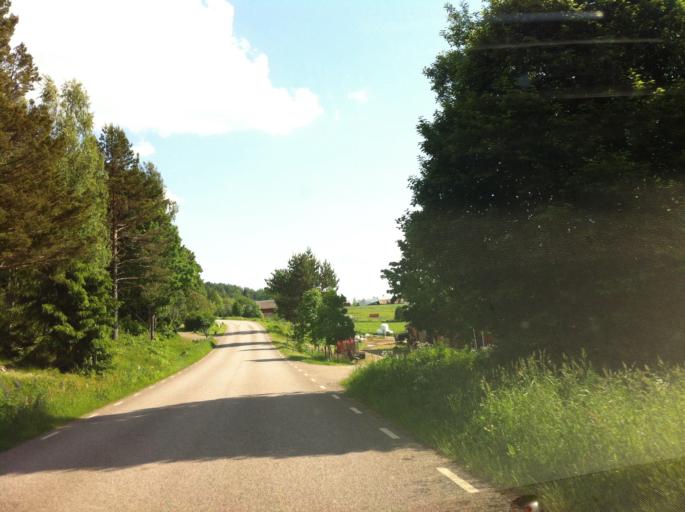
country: SE
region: Vaermland
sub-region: Kils Kommun
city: Kil
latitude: 59.6301
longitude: 13.3226
